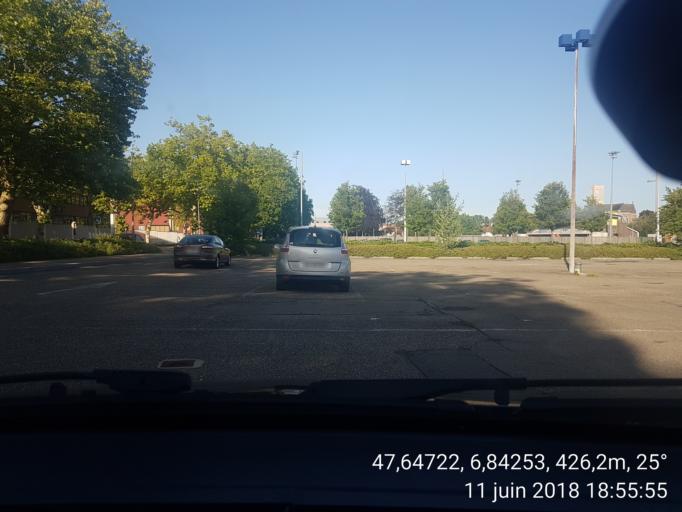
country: FR
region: Franche-Comte
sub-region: Territoire de Belfort
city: Cravanche
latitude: 47.6473
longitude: 6.8424
